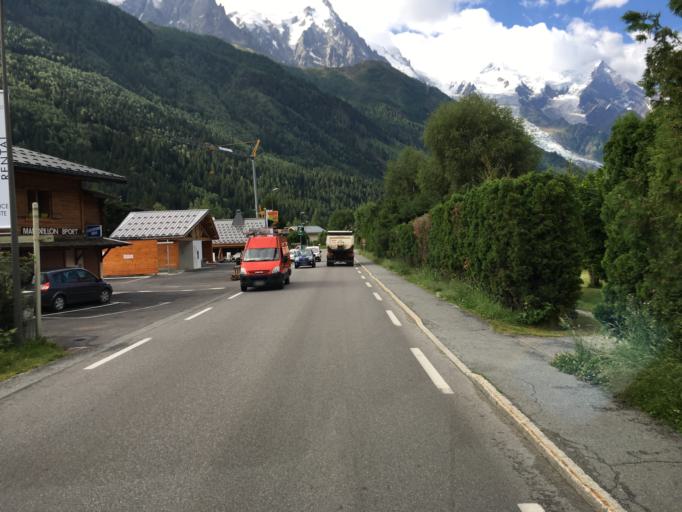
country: FR
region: Rhone-Alpes
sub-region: Departement de la Haute-Savoie
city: Chamonix-Mont-Blanc
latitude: 45.9399
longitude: 6.8879
